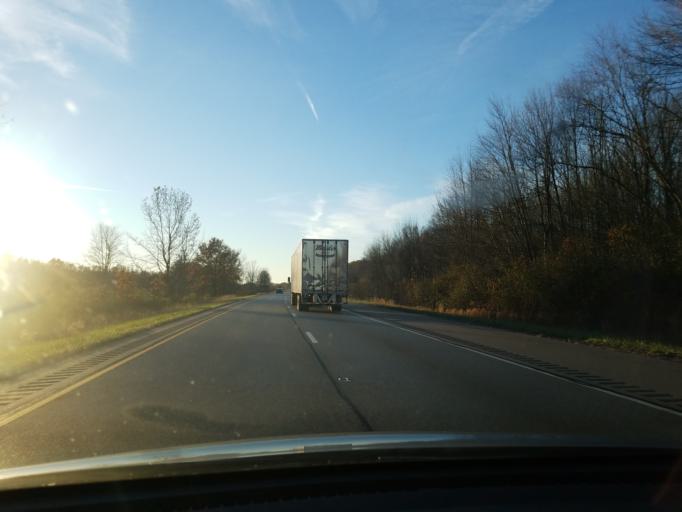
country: US
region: Indiana
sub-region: Warrick County
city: Chandler
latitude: 38.1843
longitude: -87.3690
